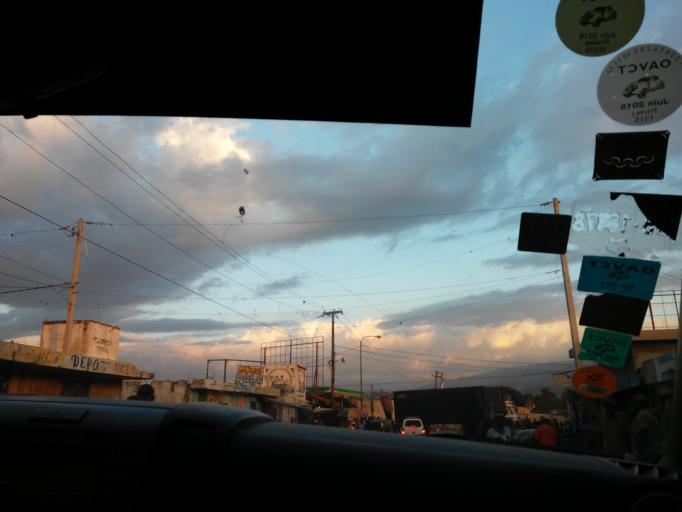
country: HT
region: Ouest
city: Port-au-Prince
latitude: 18.5631
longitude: -72.3415
